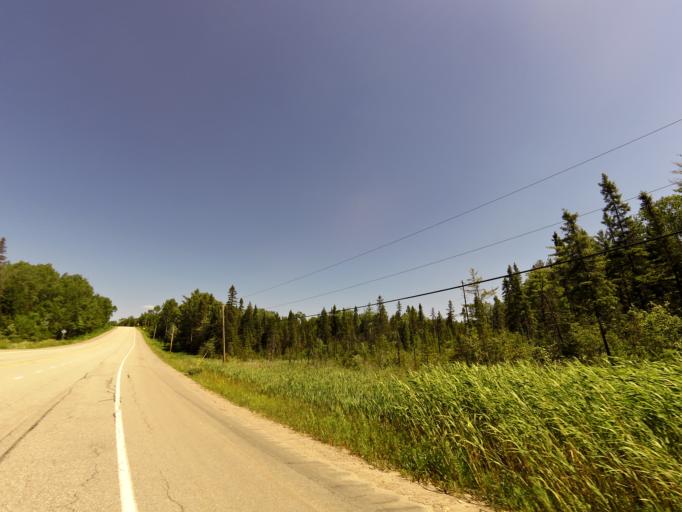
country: CA
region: Quebec
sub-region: Abitibi-Temiscamingue
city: Temiscaming
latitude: 46.7540
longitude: -79.0778
